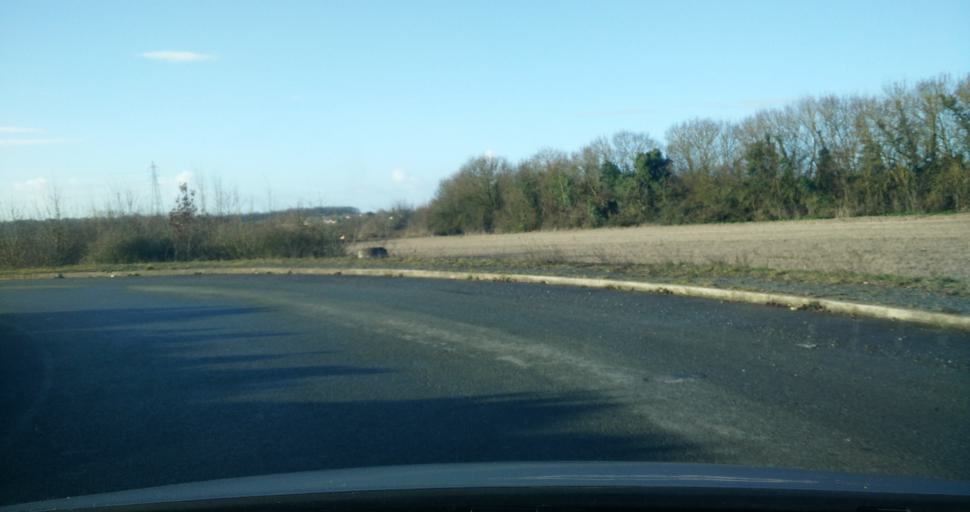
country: FR
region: Poitou-Charentes
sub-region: Departement de la Charente-Maritime
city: Saint-Xandre
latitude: 46.2048
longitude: -1.0914
